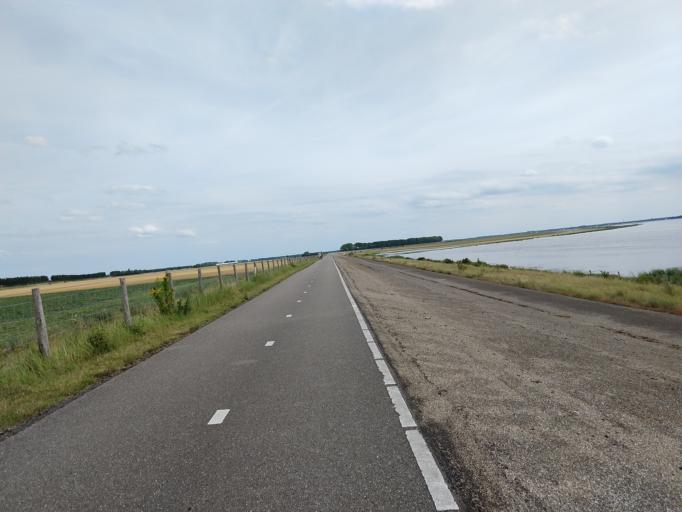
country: NL
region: North Brabant
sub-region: Gemeente Steenbergen
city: Nieuw-Vossemeer
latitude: 51.6757
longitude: 4.2141
